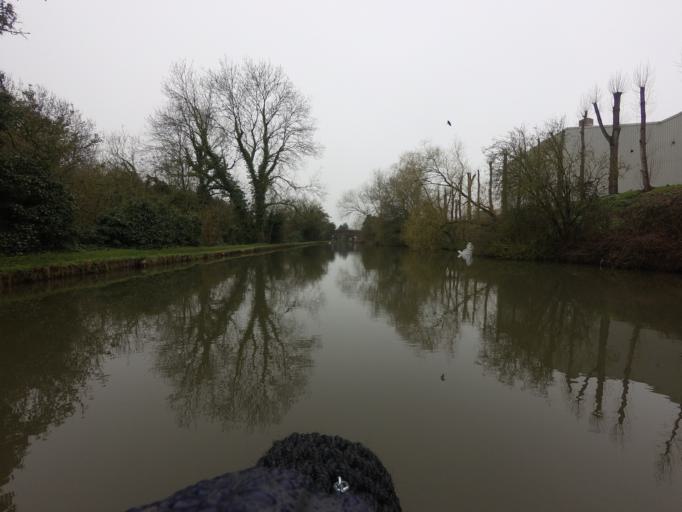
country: GB
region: England
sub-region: Milton Keynes
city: Simpson
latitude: 52.0104
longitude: -0.7161
